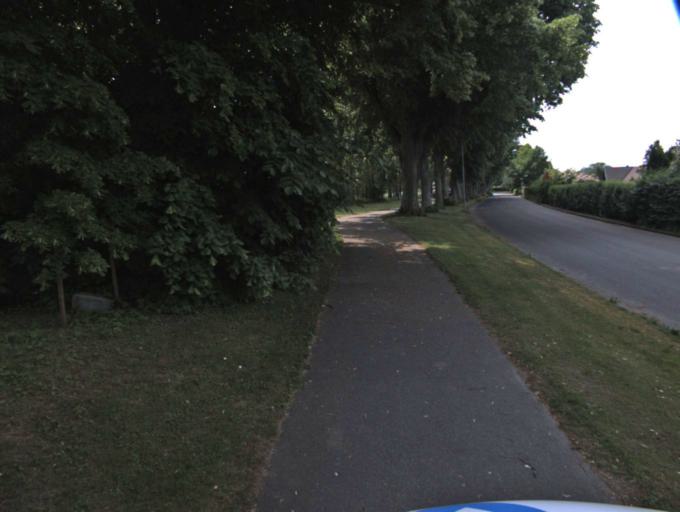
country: SE
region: Skane
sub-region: Kristianstads Kommun
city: Kristianstad
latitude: 56.0746
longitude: 14.2130
